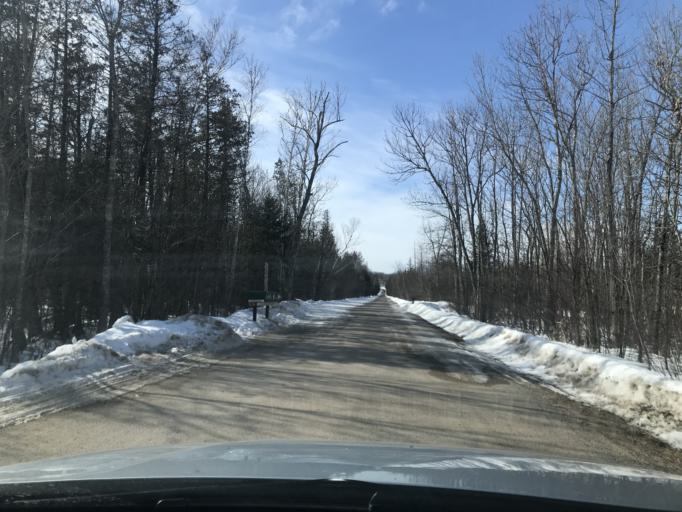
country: US
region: Wisconsin
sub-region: Marinette County
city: Peshtigo
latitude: 45.3008
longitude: -87.8239
